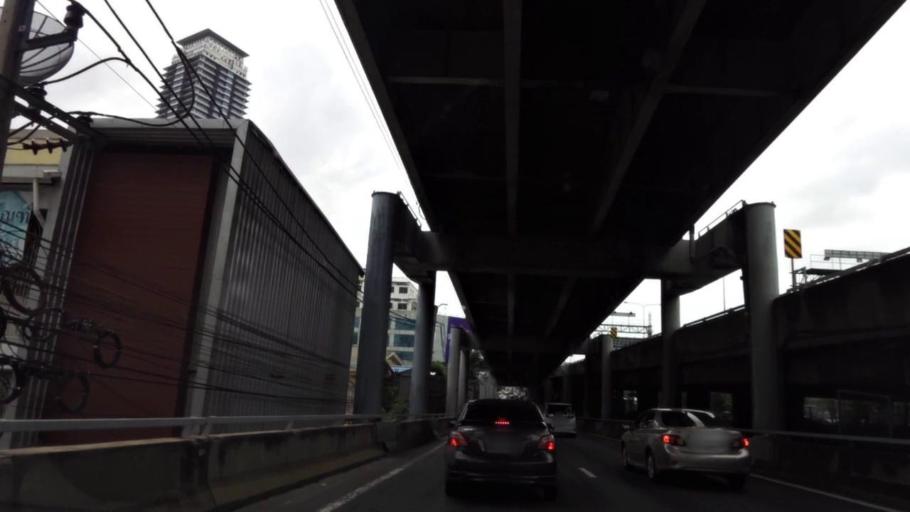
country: TH
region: Bangkok
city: Khlong Toei
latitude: 13.7204
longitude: 100.5526
